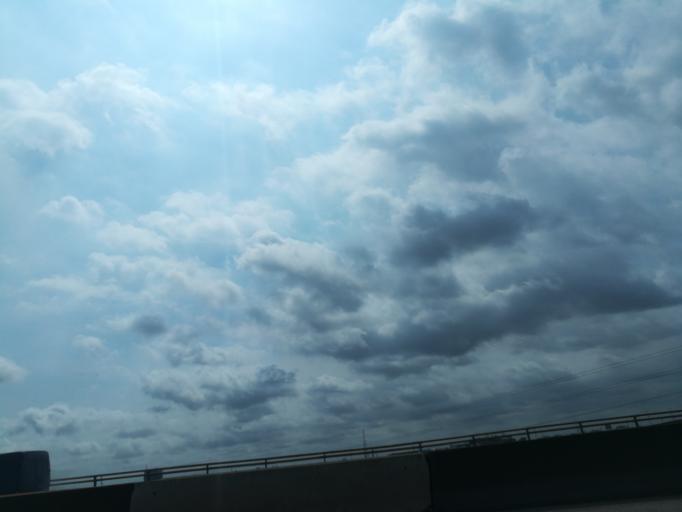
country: NG
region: Lagos
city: Ebute Metta
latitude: 6.4765
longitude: 3.3907
